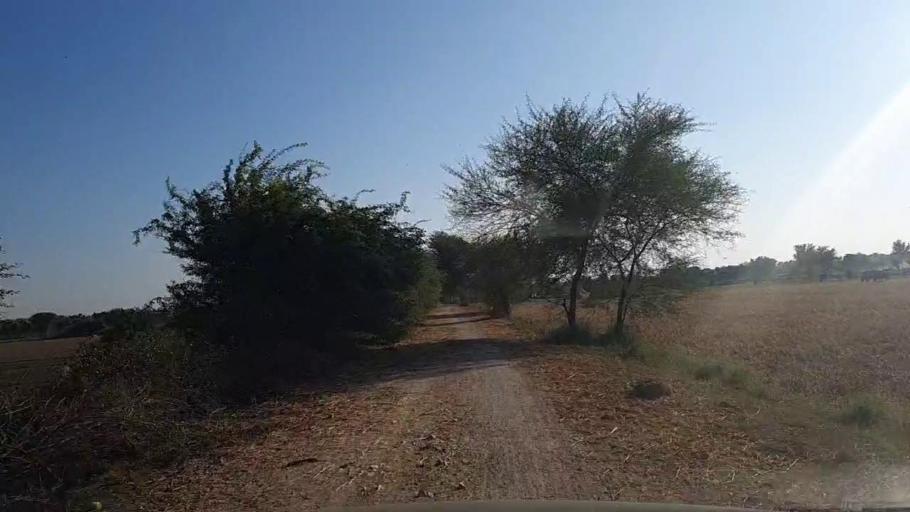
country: PK
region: Sindh
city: Mirpur Batoro
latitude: 24.6767
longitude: 68.3644
